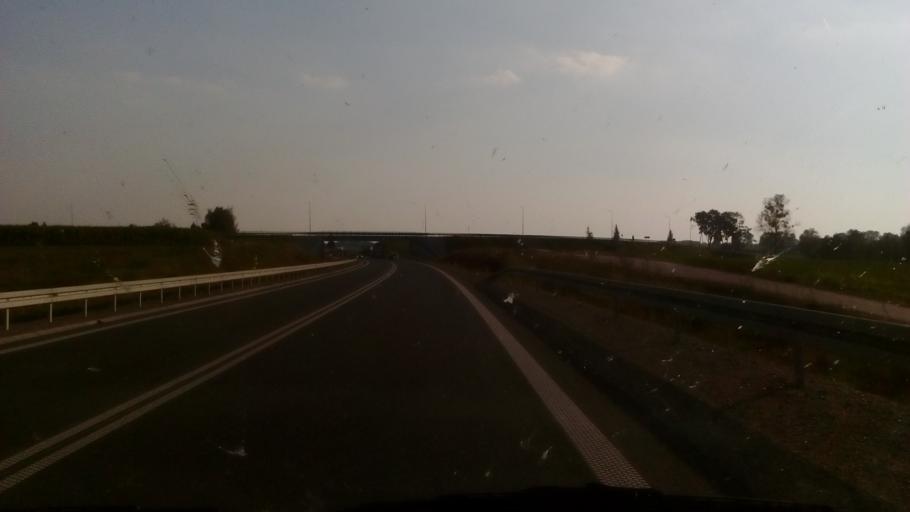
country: PL
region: Podlasie
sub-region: Powiat grajewski
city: Rajgrod
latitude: 53.7762
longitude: 22.8359
